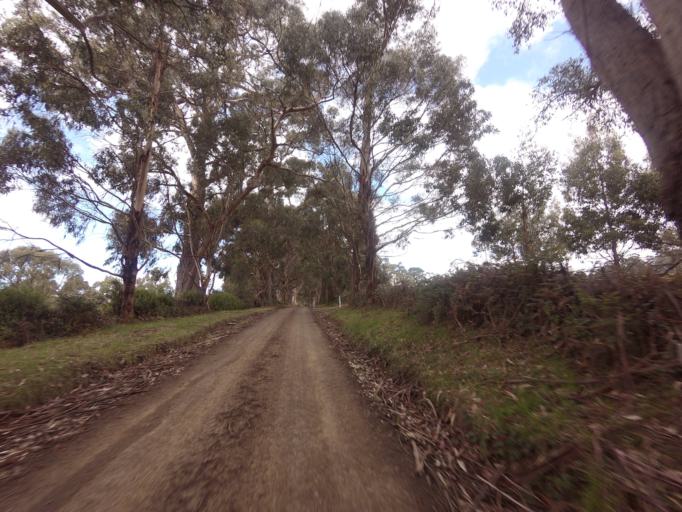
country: AU
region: Tasmania
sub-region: Huon Valley
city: Cygnet
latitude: -43.4093
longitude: 147.0187
